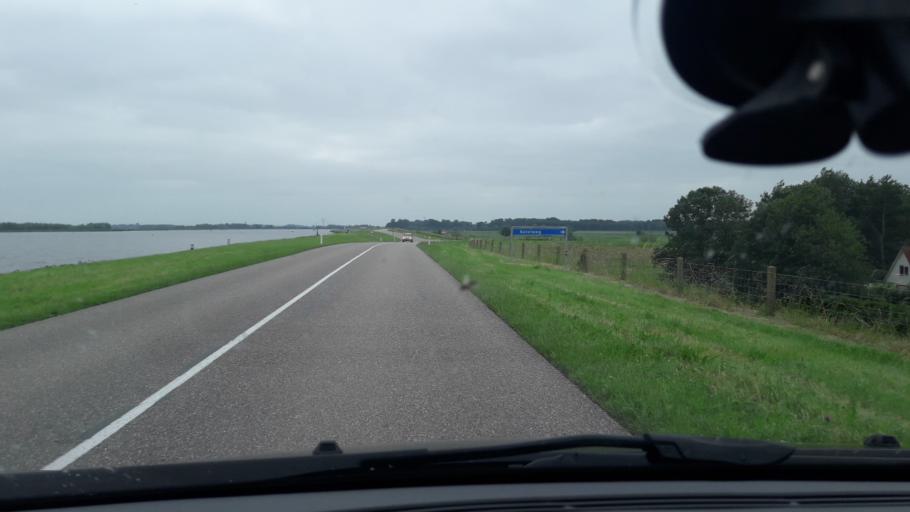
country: NL
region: Flevoland
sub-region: Gemeente Dronten
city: Dronten
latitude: 52.5790
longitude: 5.7664
